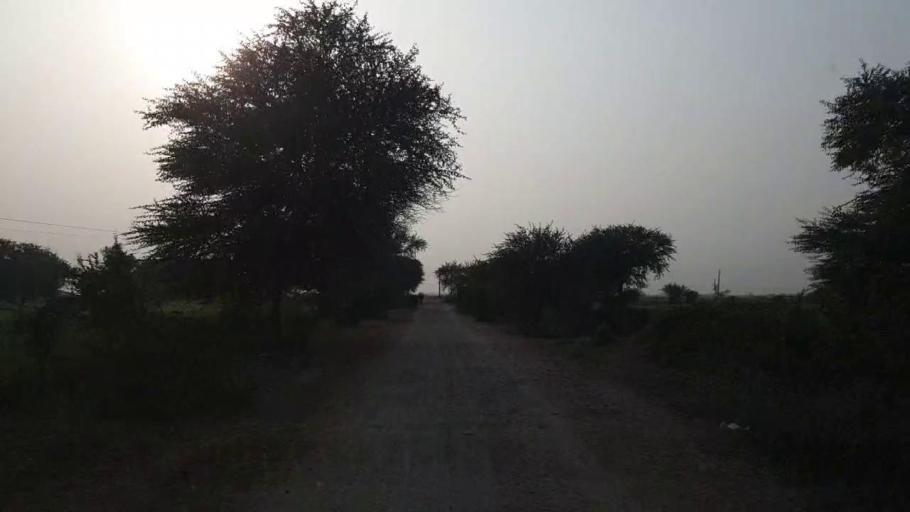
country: PK
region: Sindh
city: Mirpur Batoro
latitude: 24.6605
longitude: 68.3768
